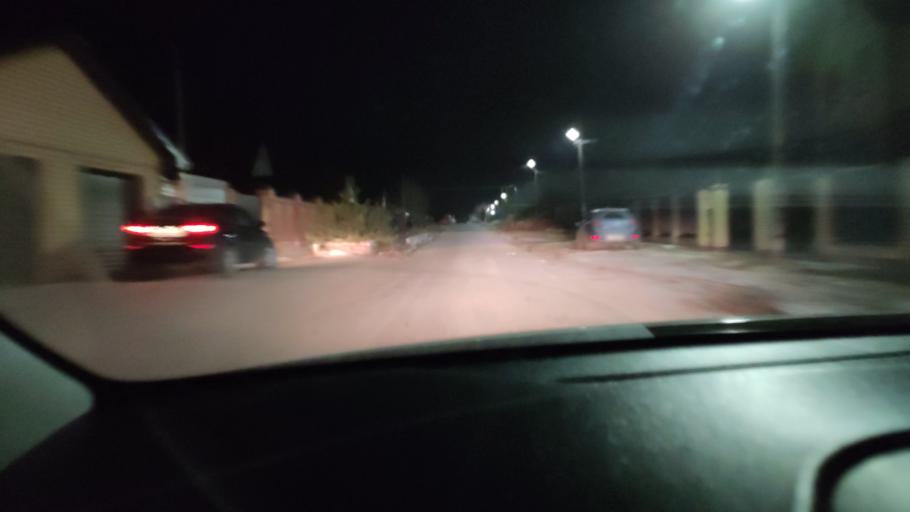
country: RU
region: Tatarstan
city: Stolbishchi
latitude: 55.7622
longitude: 49.2582
